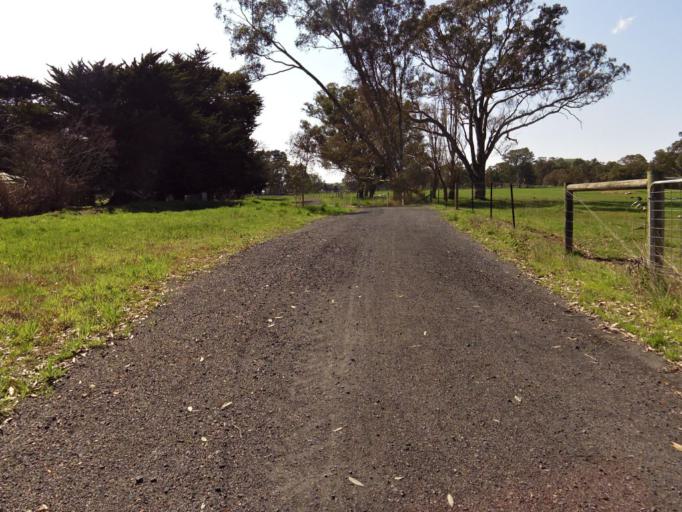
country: AU
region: Victoria
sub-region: Murrindindi
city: Alexandra
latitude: -37.1110
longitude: 145.6105
